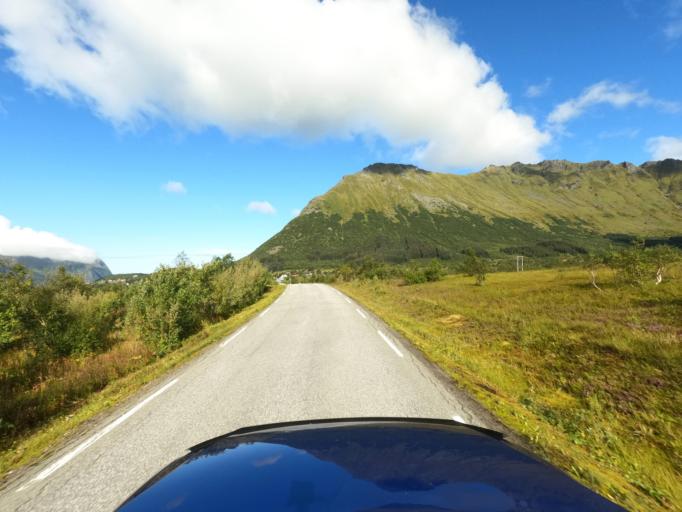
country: NO
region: Nordland
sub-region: Vagan
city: Kabelvag
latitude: 68.2812
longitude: 14.3516
